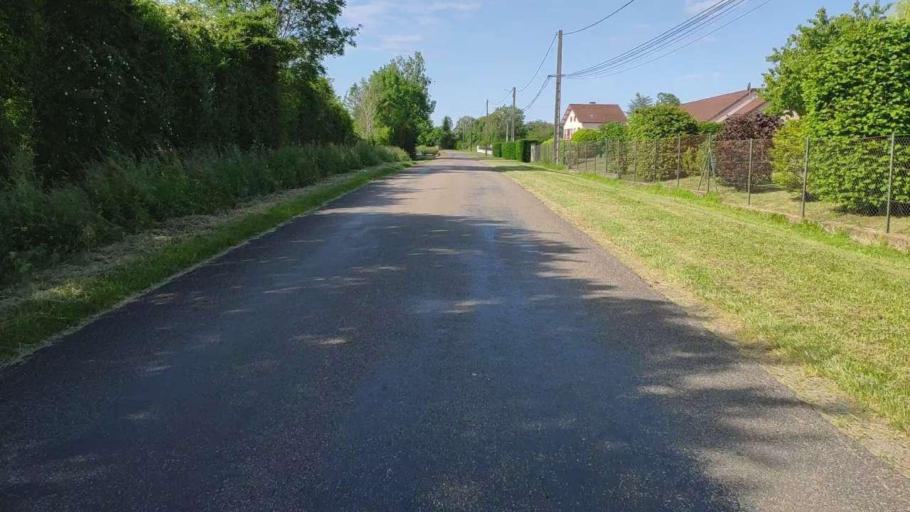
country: FR
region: Franche-Comte
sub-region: Departement du Jura
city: Bletterans
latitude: 46.7151
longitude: 5.4715
